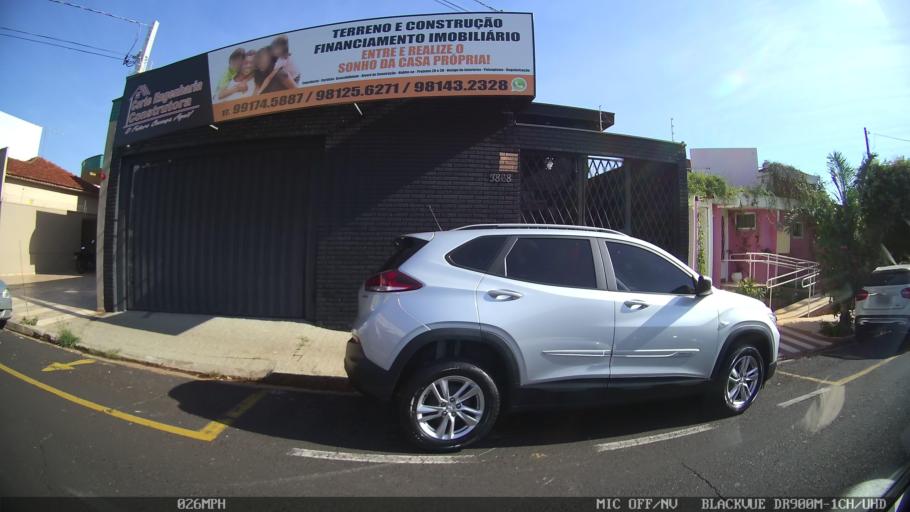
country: BR
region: Sao Paulo
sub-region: Sao Jose Do Rio Preto
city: Sao Jose do Rio Preto
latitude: -20.8198
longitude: -49.3786
